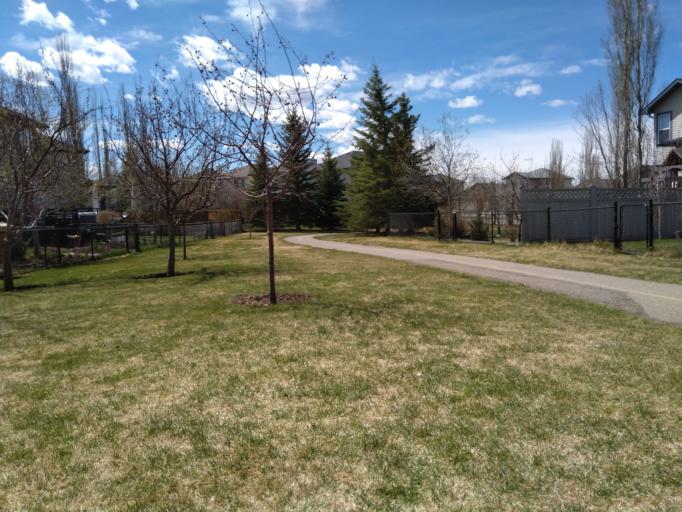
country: CA
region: Alberta
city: Calgary
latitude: 51.1150
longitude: -114.2398
